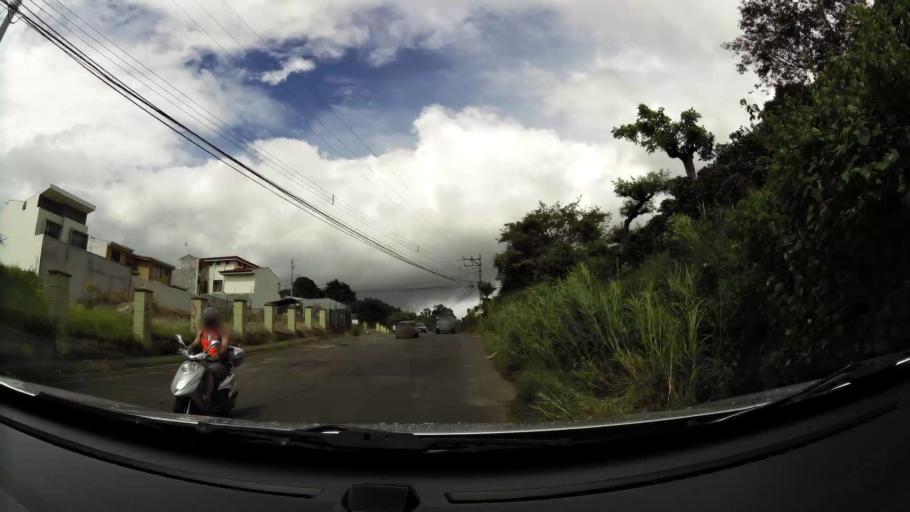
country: CR
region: Cartago
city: Tres Rios
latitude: 9.9118
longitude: -83.9885
